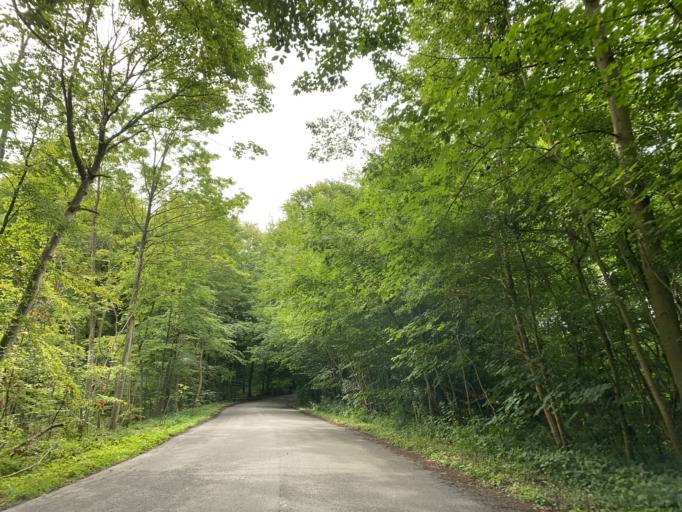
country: DK
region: South Denmark
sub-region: Sonderborg Kommune
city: Sonderborg
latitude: 54.9104
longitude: 9.8309
